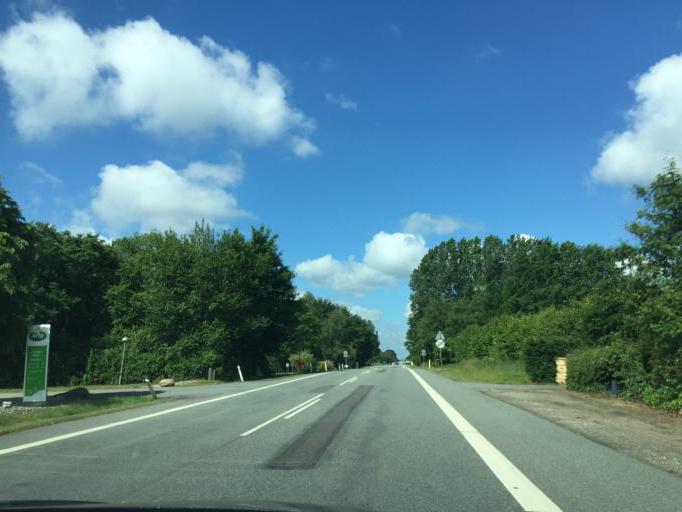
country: DK
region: South Denmark
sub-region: Fredericia Kommune
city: Taulov
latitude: 55.5319
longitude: 9.6348
